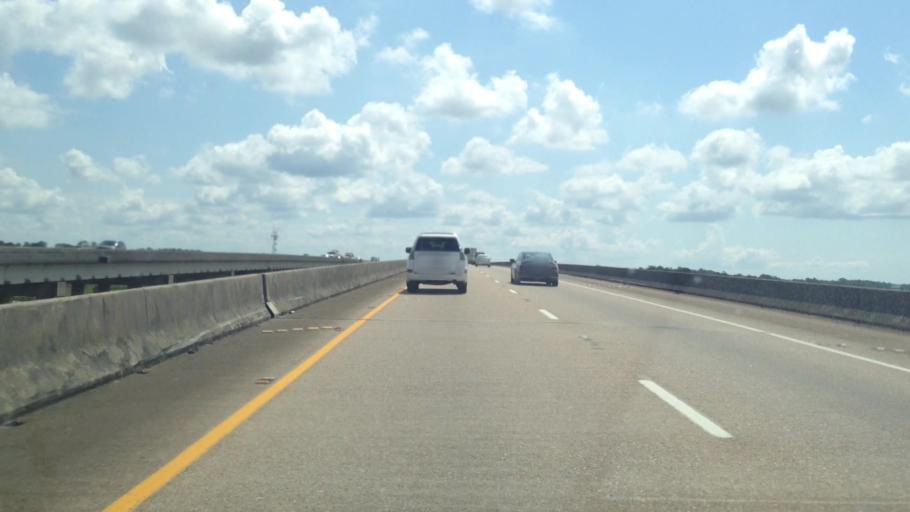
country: US
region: Mississippi
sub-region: Jackson County
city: Escatawpa
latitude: 30.4380
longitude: -88.5611
